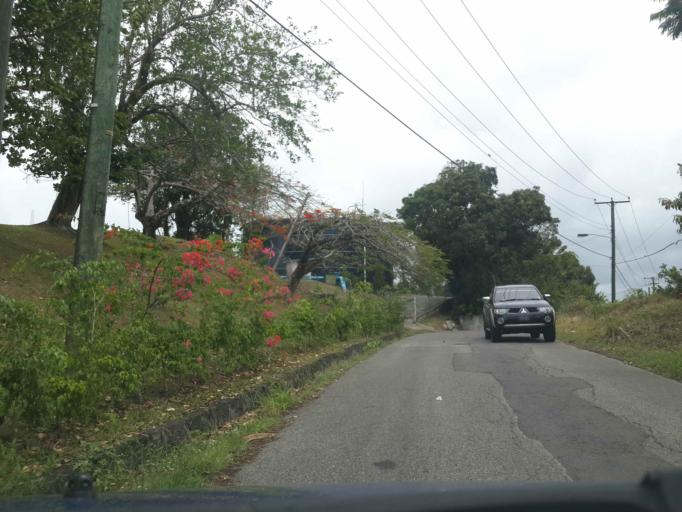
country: LC
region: Castries Quarter
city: Castries
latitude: 13.9964
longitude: -60.9936
